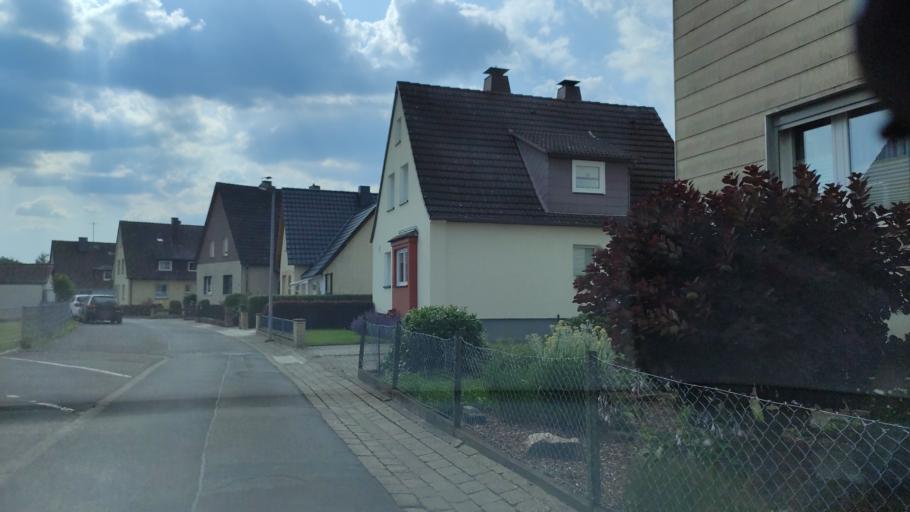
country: DE
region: Lower Saxony
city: Holzminden
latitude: 51.8303
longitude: 9.4671
